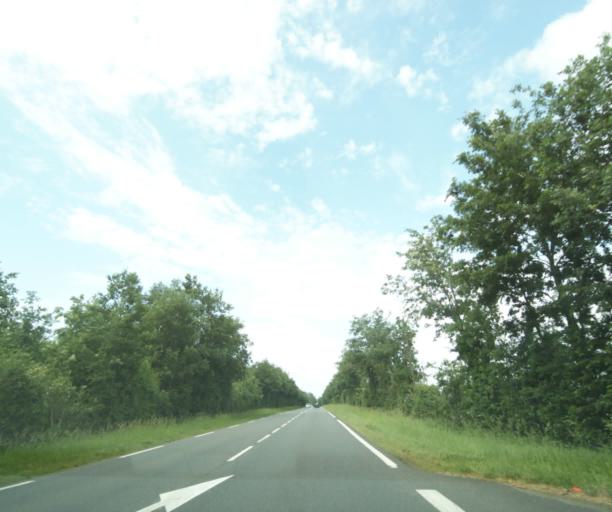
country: FR
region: Pays de la Loire
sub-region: Departement de Maine-et-Loire
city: Montreuil-Bellay
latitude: 47.1582
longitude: -0.1451
